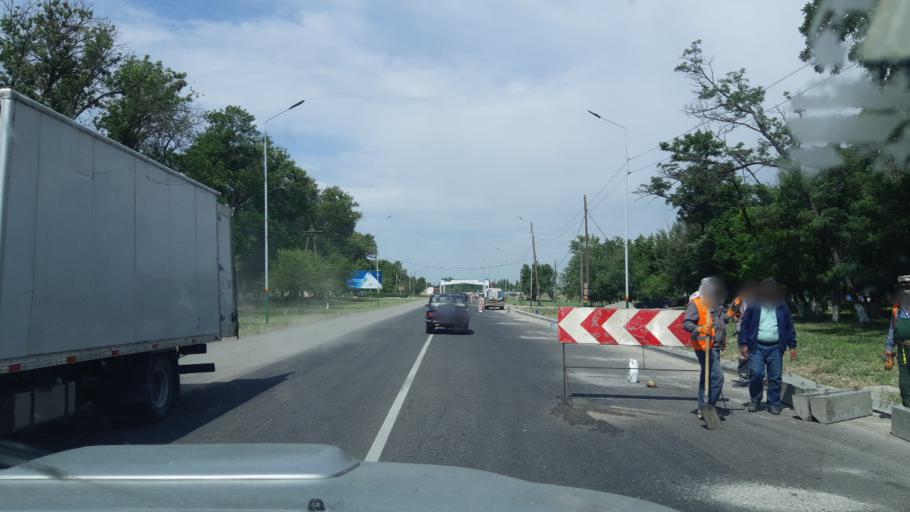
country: KZ
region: Ongtustik Qazaqstan
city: Turar Ryskulov
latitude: 42.5490
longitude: 70.3088
